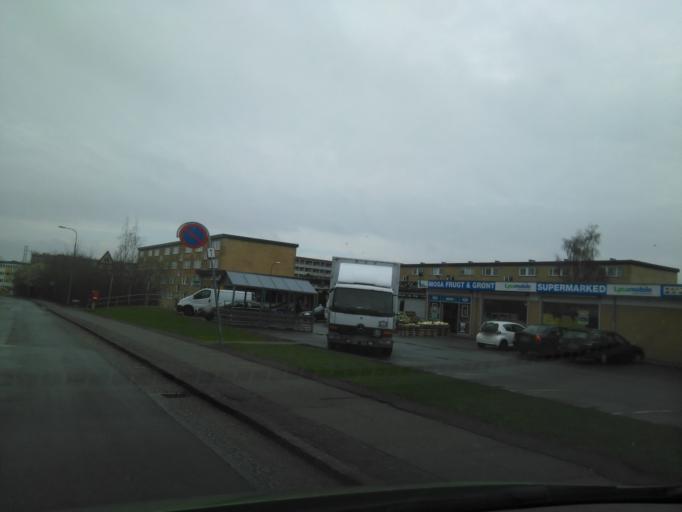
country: DK
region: Central Jutland
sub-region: Arhus Kommune
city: Stavtrup
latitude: 56.1583
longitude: 10.1299
